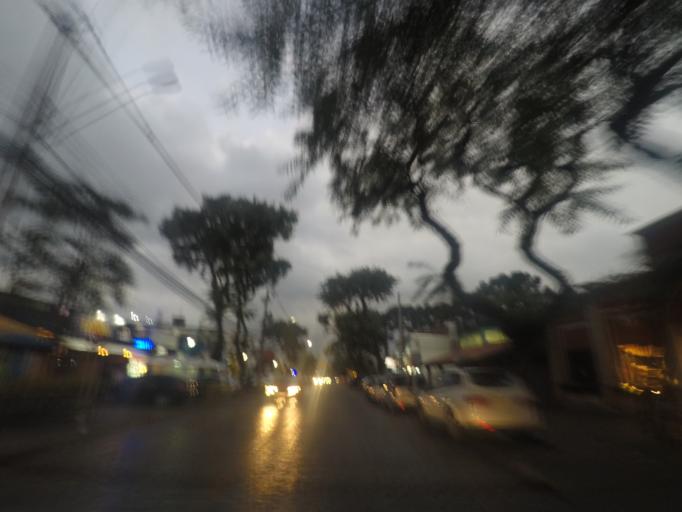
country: BR
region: Parana
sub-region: Curitiba
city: Curitiba
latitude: -25.4041
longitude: -49.3286
